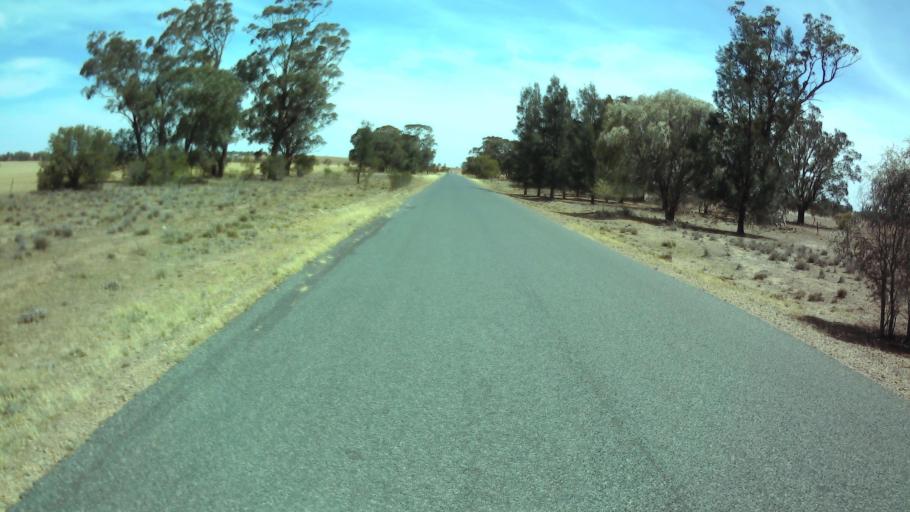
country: AU
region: New South Wales
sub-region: Weddin
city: Grenfell
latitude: -33.8812
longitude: 147.7428
